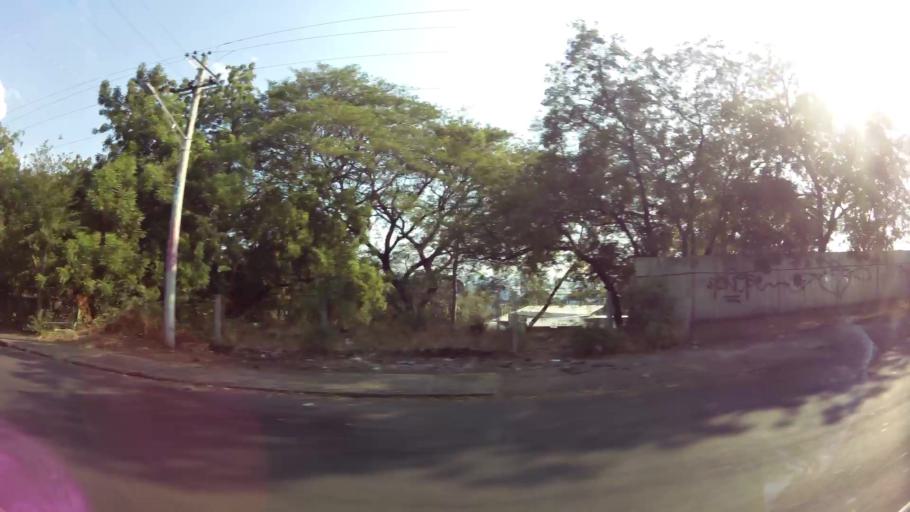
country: NI
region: Managua
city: Managua
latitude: 12.1376
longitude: -86.2746
